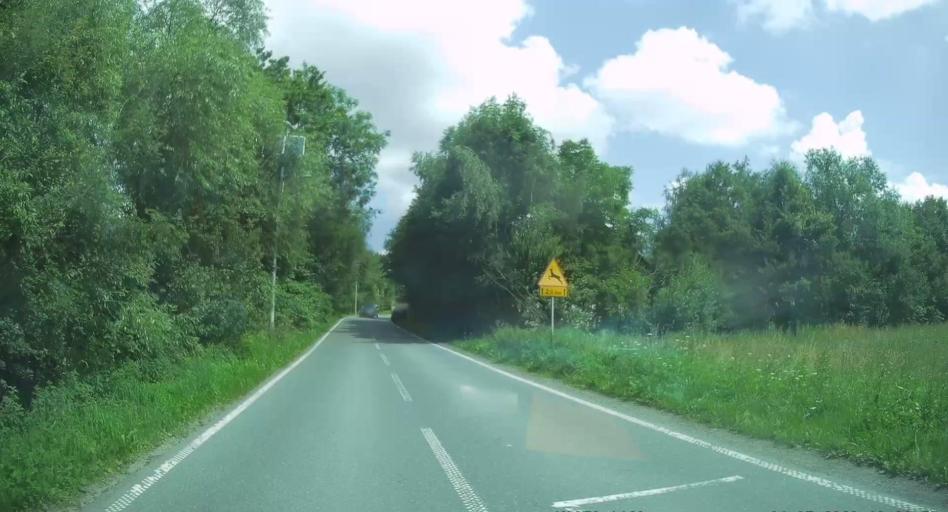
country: PL
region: Lesser Poland Voivodeship
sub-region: Powiat nowosadecki
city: Korzenna
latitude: 49.7036
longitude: 20.7624
